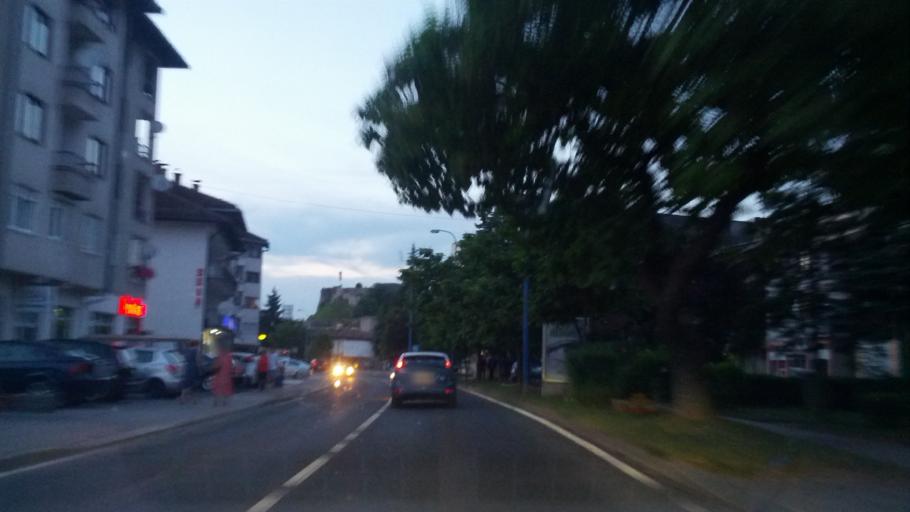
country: BA
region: Federation of Bosnia and Herzegovina
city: Bosanska Krupa
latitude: 44.8818
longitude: 16.1538
